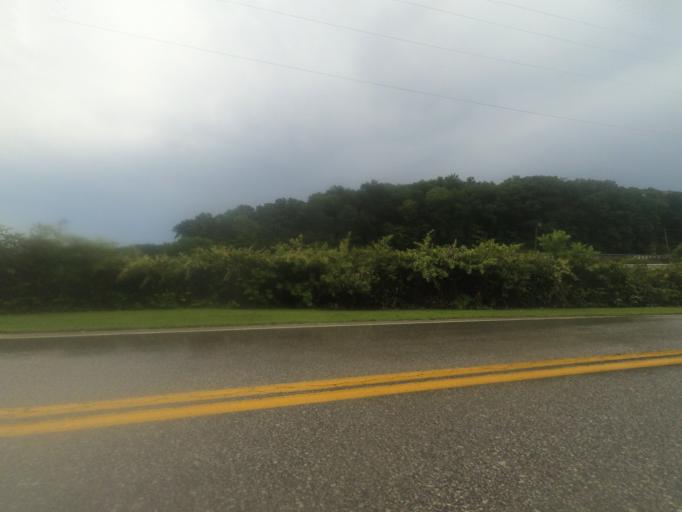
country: US
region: West Virginia
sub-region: Cabell County
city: Huntington
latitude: 38.3853
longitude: -82.3962
